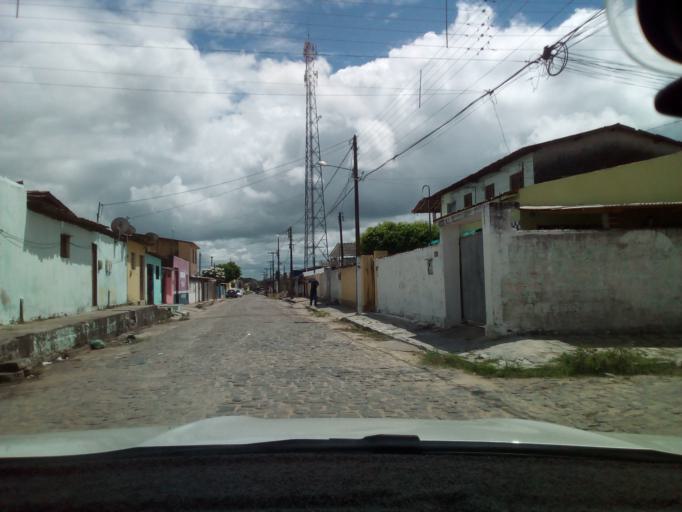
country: BR
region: Paraiba
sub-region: Bayeux
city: Bayeux
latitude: -7.1321
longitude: -34.9384
